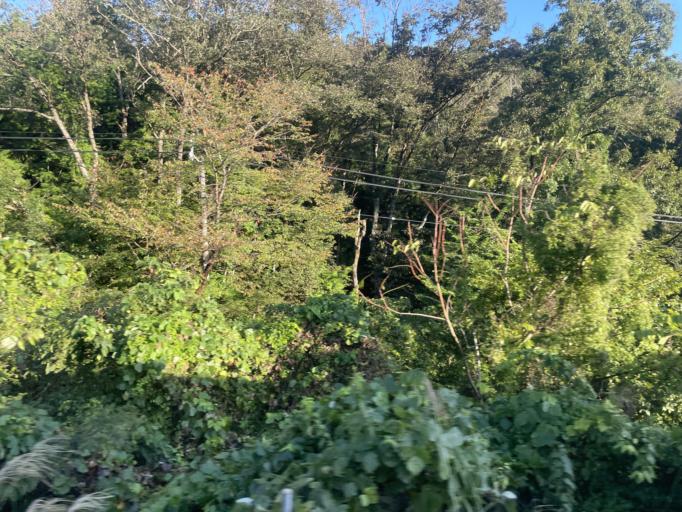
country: JP
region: Mie
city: Nabari
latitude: 34.5850
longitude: 136.0544
